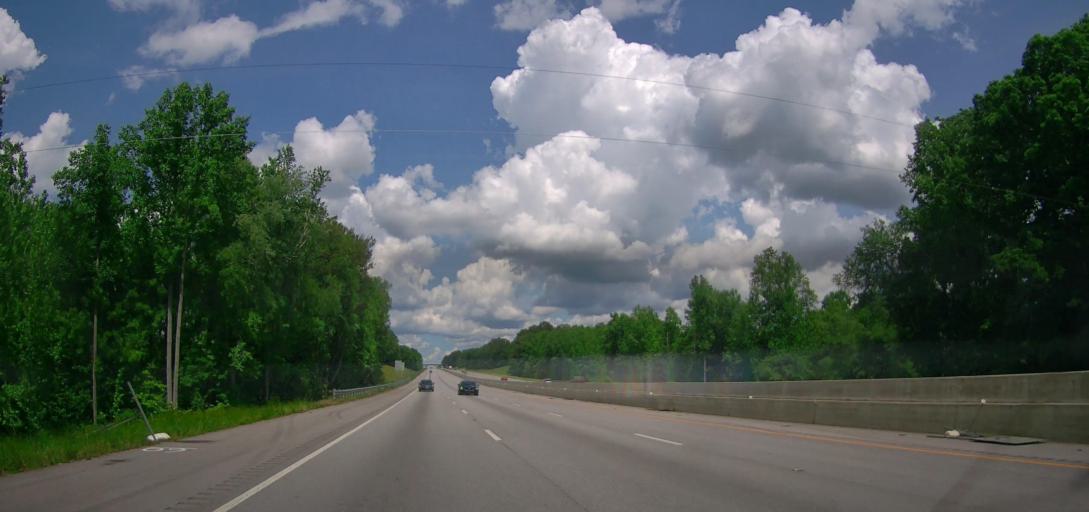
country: US
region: Georgia
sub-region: Haralson County
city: Tallapoosa
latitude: 33.6592
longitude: -85.3971
